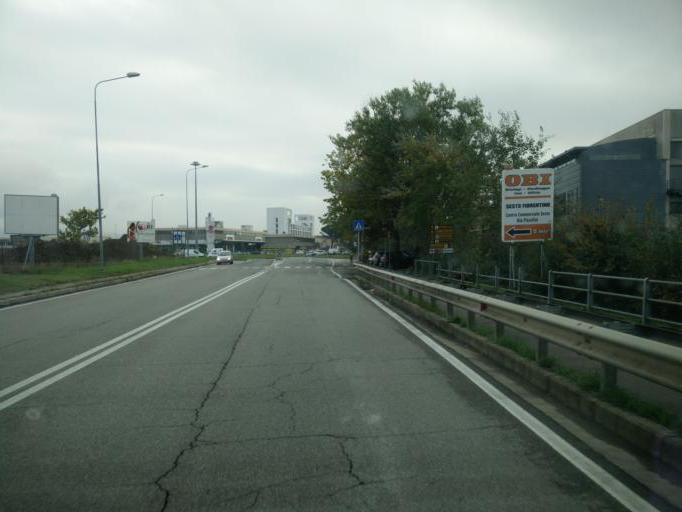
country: IT
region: Tuscany
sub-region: Province of Florence
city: Mantignano-Ugnano
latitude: 43.8073
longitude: 11.1759
